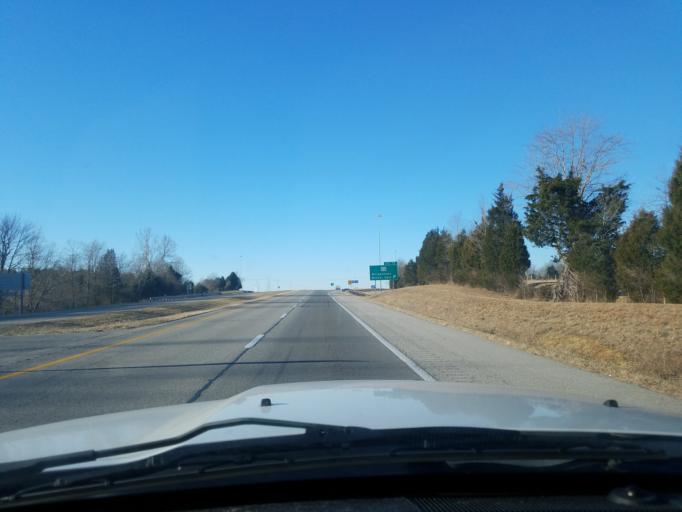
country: US
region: Kentucky
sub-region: Ohio County
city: Beaver Dam
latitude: 37.3706
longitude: -86.8370
